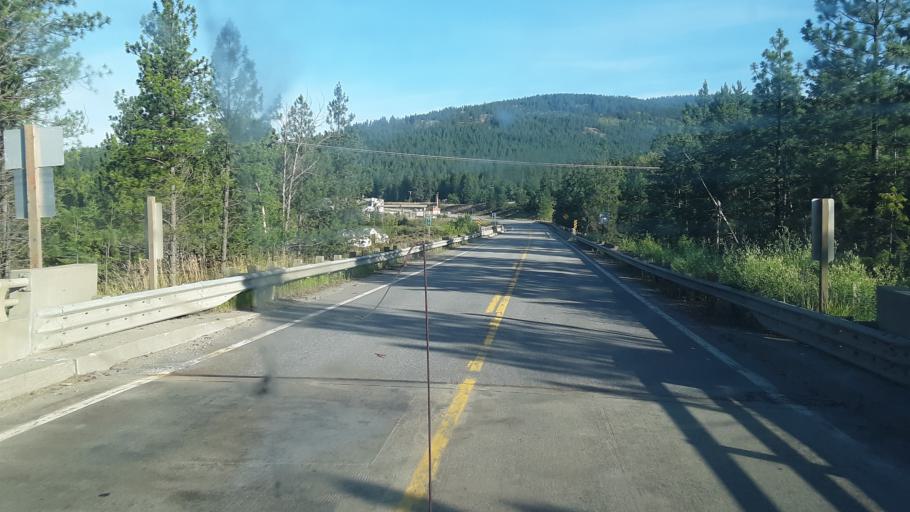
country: US
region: Idaho
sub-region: Boundary County
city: Bonners Ferry
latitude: 48.7299
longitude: -116.1797
